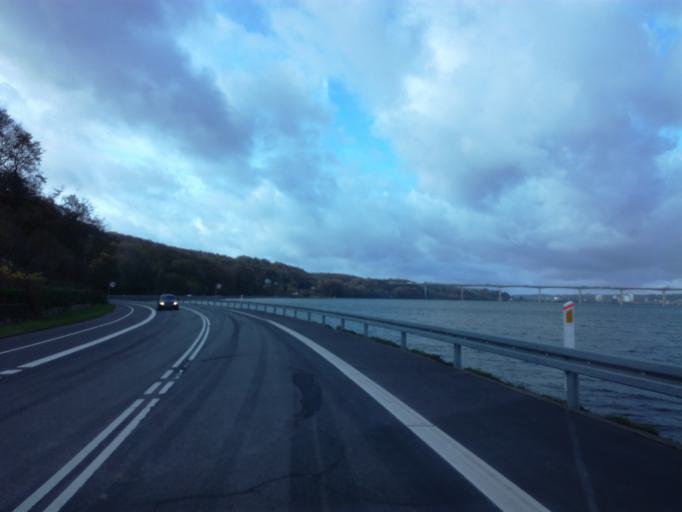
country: DK
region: South Denmark
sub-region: Vejle Kommune
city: Vejle
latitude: 55.6912
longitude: 9.5980
